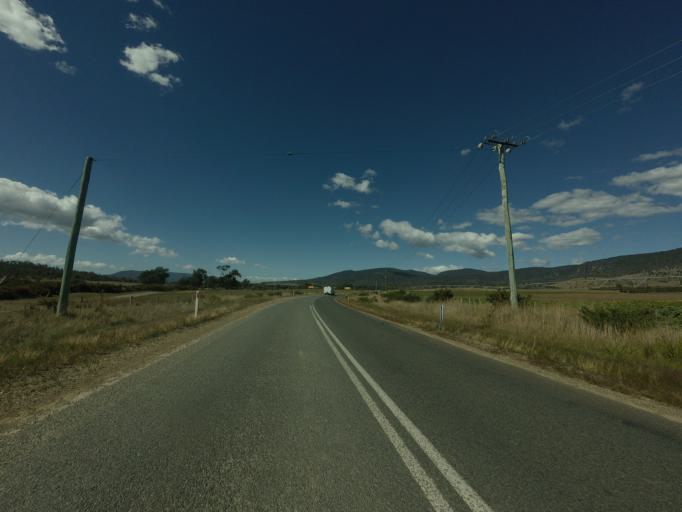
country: AU
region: Tasmania
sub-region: Break O'Day
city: St Helens
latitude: -41.6459
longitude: 147.9420
